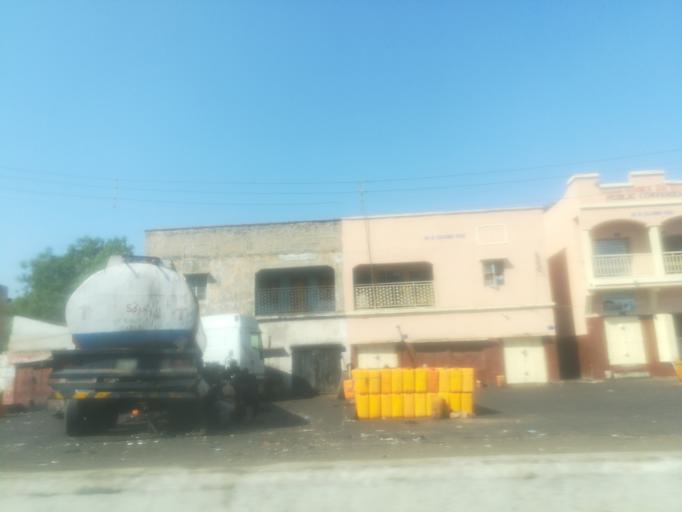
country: NG
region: Kano
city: Kano
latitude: 12.0136
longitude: 8.5325
